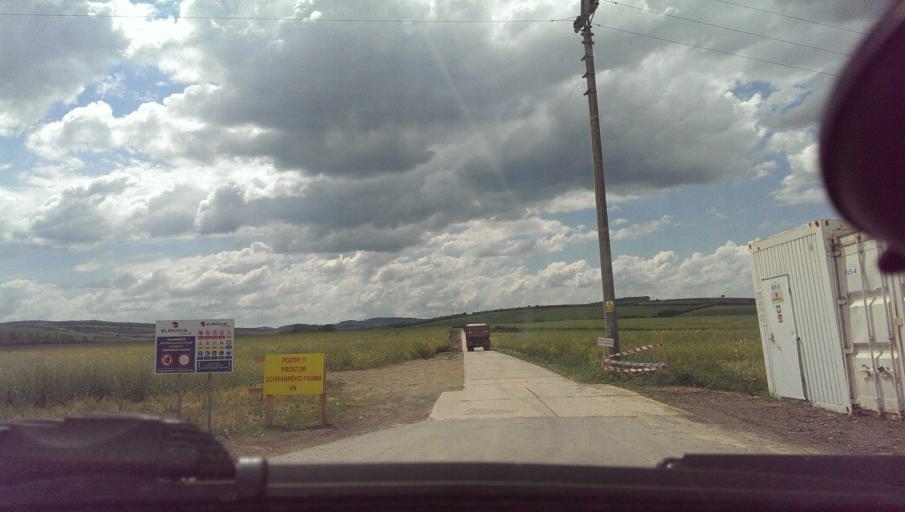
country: CZ
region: Zlin
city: Dolni Nemci
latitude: 48.9673
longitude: 17.5988
